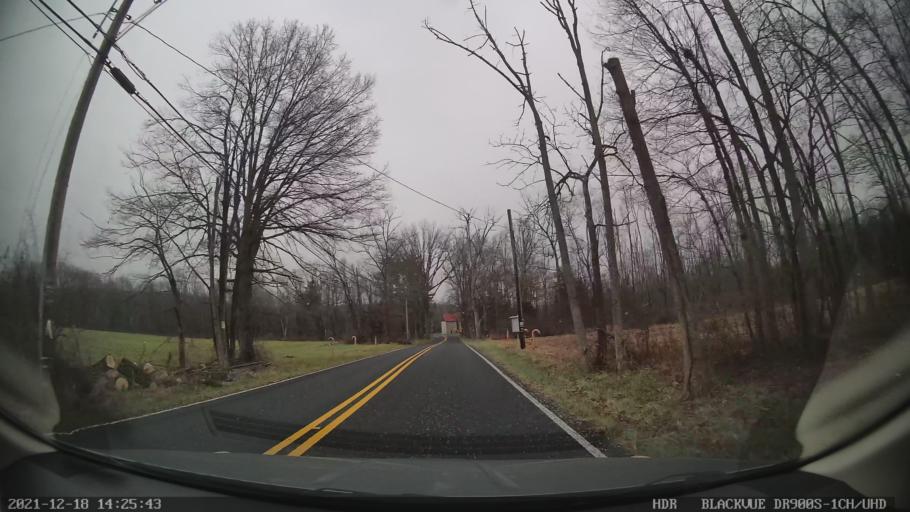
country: US
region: Pennsylvania
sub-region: Berks County
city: Oley
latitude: 40.4132
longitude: -75.7401
